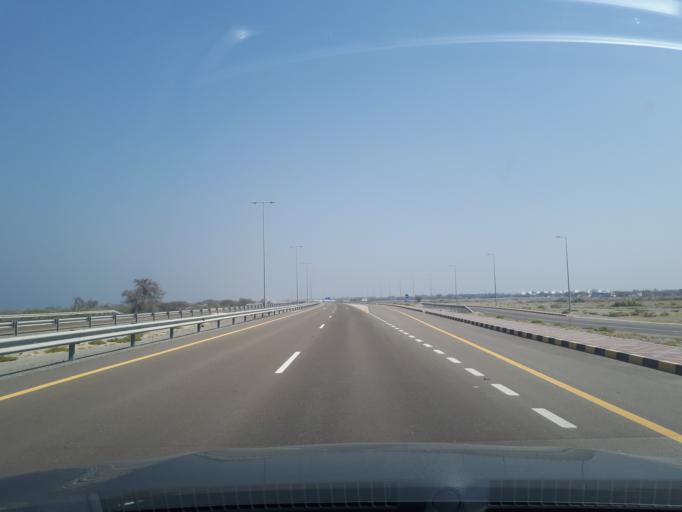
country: AE
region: Al Fujayrah
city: Al Fujayrah
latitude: 24.9265
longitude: 56.3850
